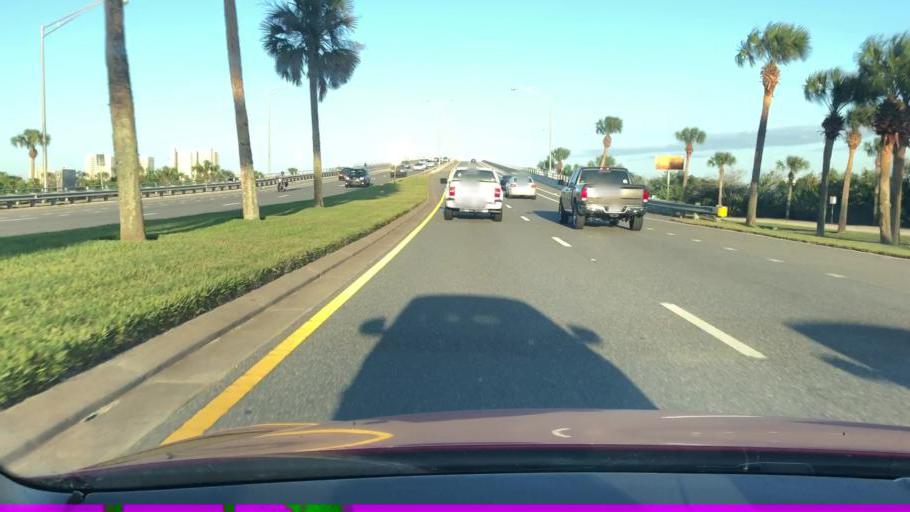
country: US
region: Florida
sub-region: Volusia County
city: Port Orange
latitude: 29.1464
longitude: -80.9796
